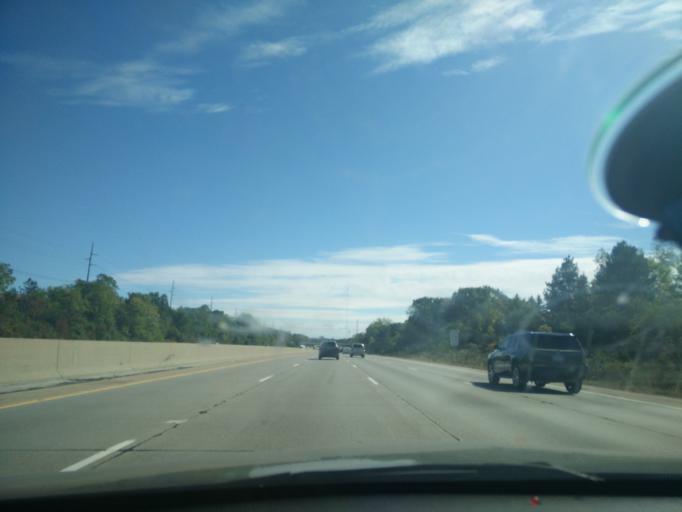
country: US
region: Michigan
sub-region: Oakland County
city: Farmington Hills
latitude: 42.4949
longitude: -83.3453
